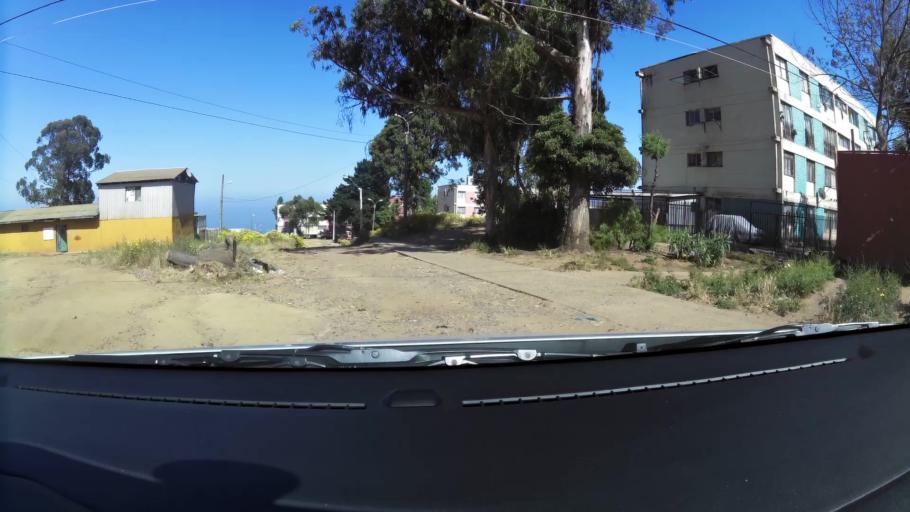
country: CL
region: Valparaiso
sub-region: Provincia de Valparaiso
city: Valparaiso
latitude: -33.0512
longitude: -71.6501
